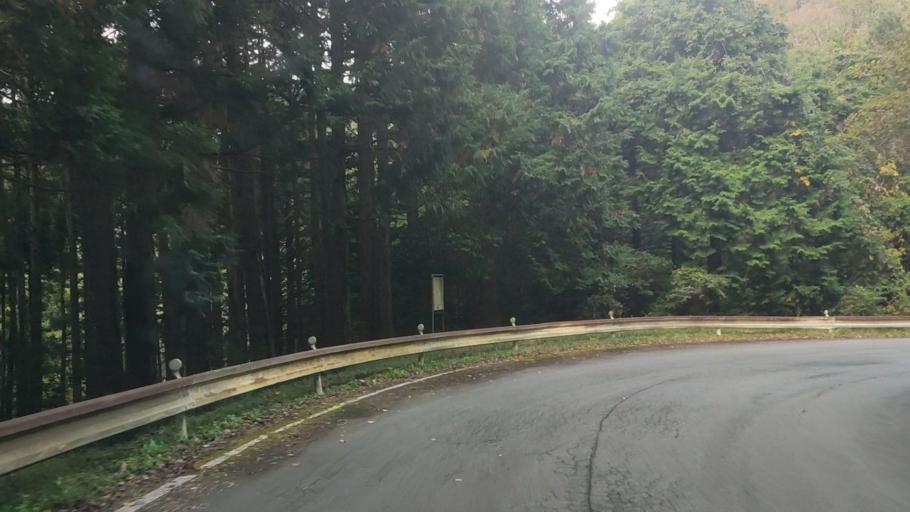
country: JP
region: Shizuoka
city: Ito
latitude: 34.9555
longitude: 139.0514
